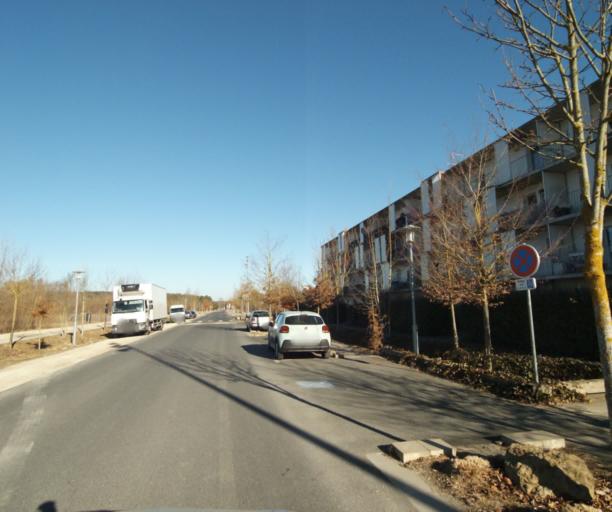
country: FR
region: Lorraine
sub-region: Departement de Meurthe-et-Moselle
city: Maxeville
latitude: 48.7031
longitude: 6.1510
